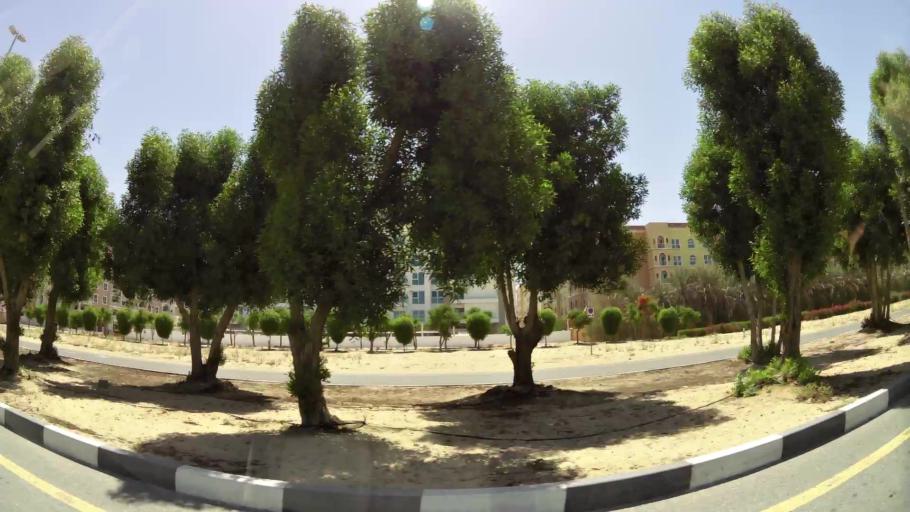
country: AE
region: Dubai
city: Dubai
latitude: 24.9894
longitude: 55.2003
